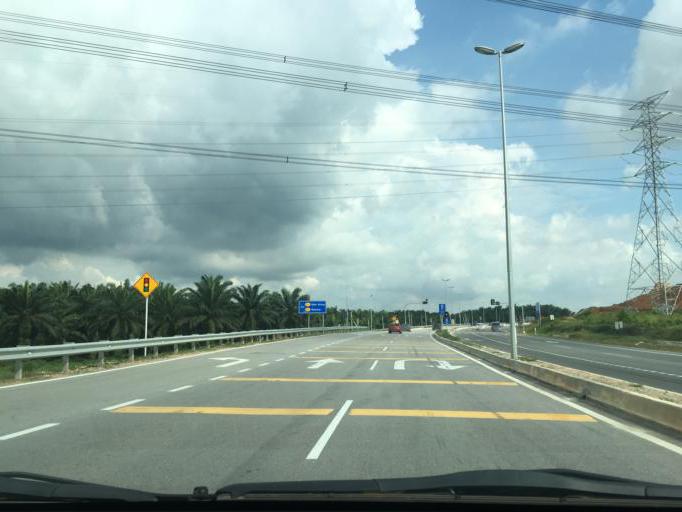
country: MY
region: Selangor
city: Batu Arang
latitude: 3.2976
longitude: 101.4393
